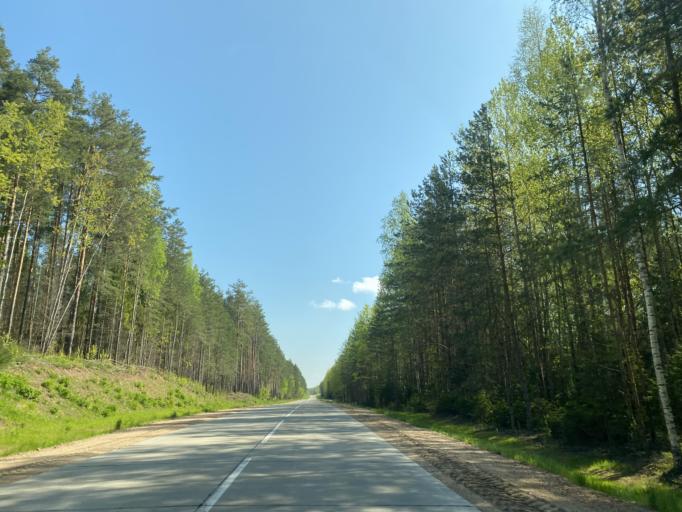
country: BY
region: Minsk
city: Horad Barysaw
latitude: 54.1720
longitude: 28.5225
